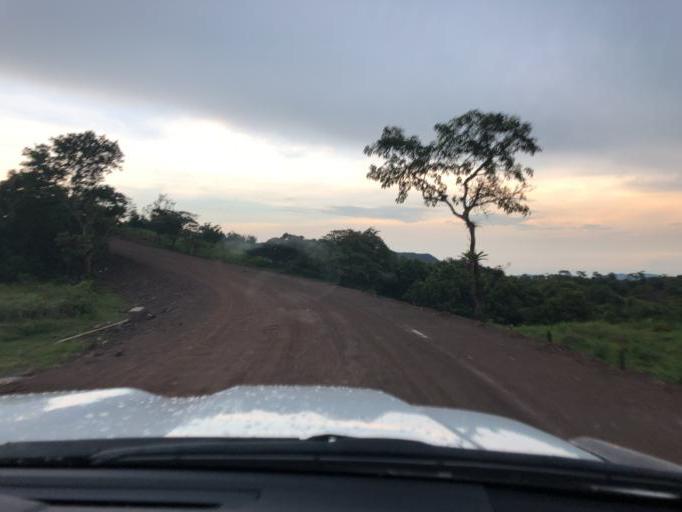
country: NI
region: Chontales
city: La Libertad
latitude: 12.1940
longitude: -85.1775
